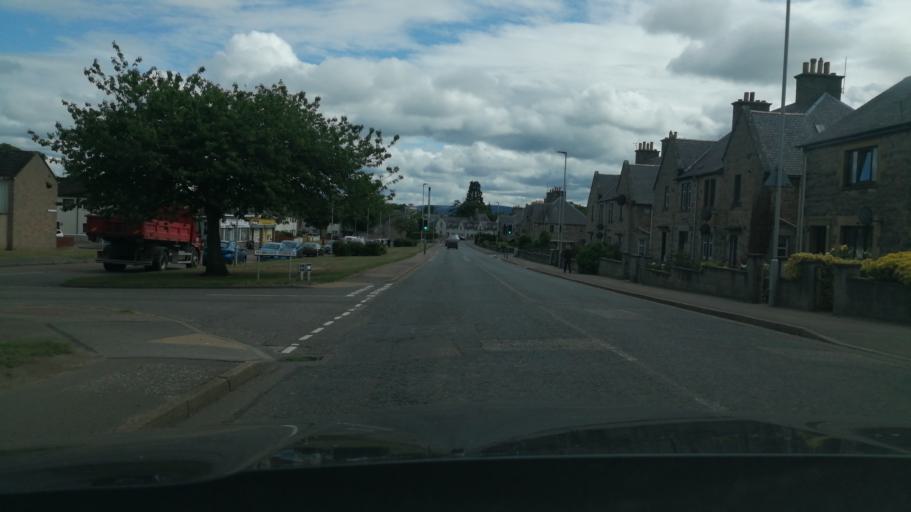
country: GB
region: Scotland
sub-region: Moray
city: Elgin
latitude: 57.6541
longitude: -3.3009
